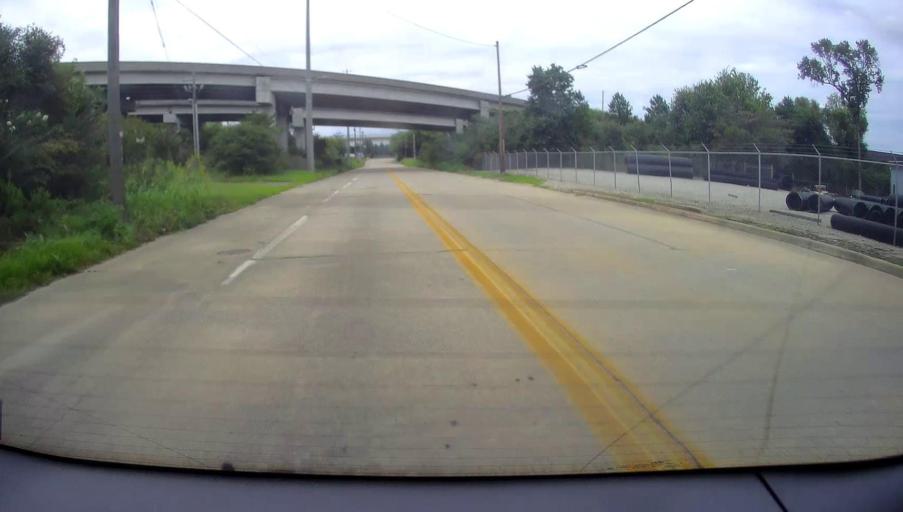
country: US
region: Georgia
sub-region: Bibb County
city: Macon
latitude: 32.8145
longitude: -83.6325
